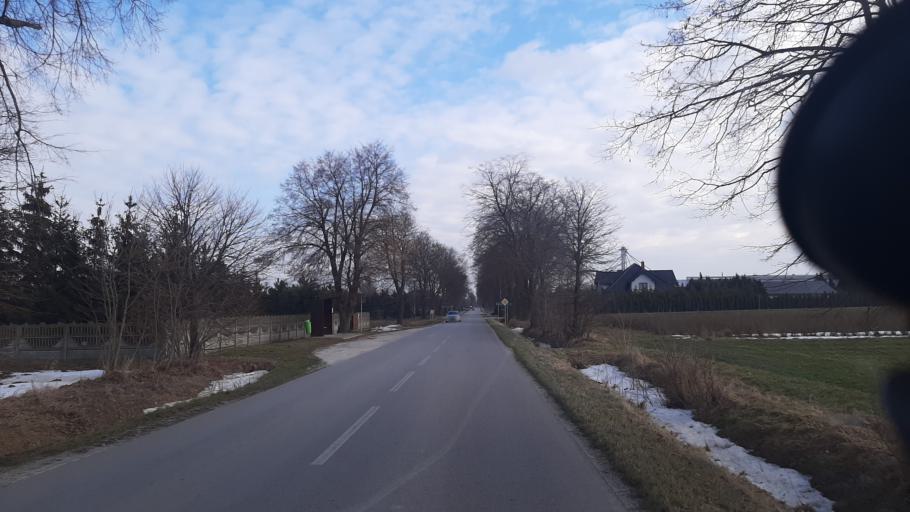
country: PL
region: Lublin Voivodeship
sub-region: Powiat lubartowski
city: Uscimow Stary
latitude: 51.4806
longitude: 22.9076
